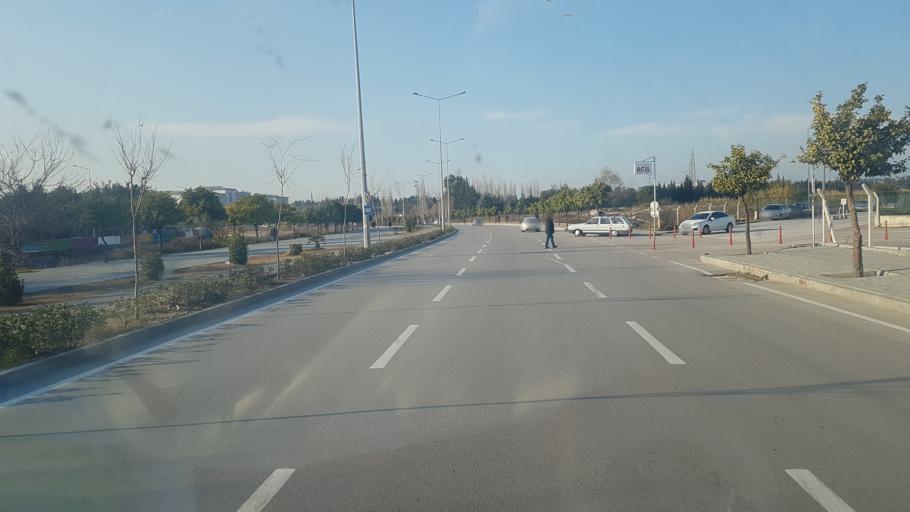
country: TR
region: Adana
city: Adana
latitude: 37.0101
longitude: 35.3530
